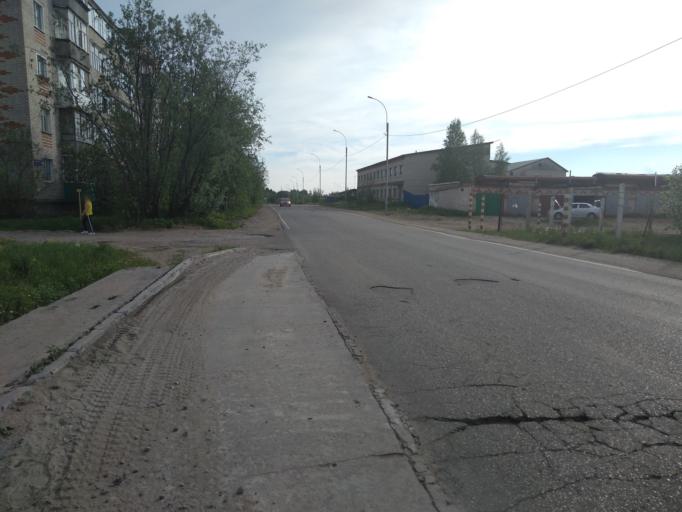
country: RU
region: Komi Republic
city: Pechora
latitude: 65.1477
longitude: 57.2123
